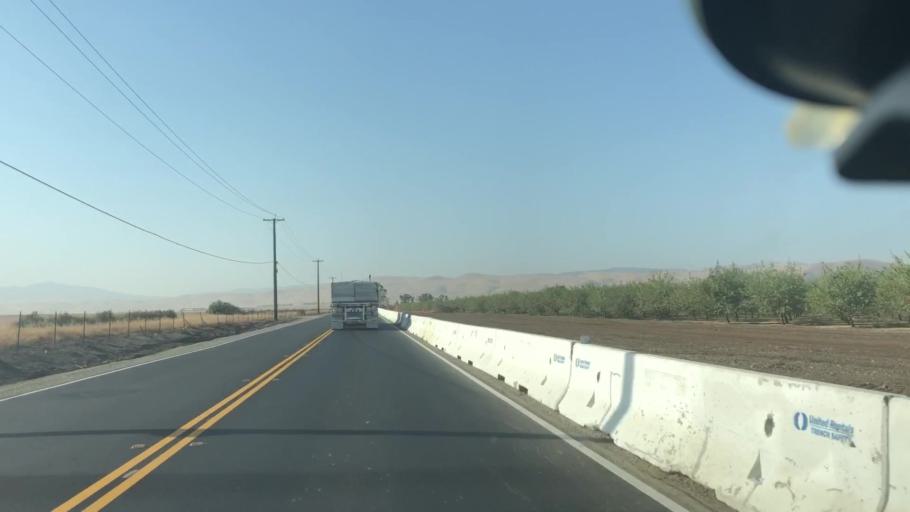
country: US
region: California
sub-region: San Joaquin County
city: Tracy
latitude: 37.6862
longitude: -121.4528
